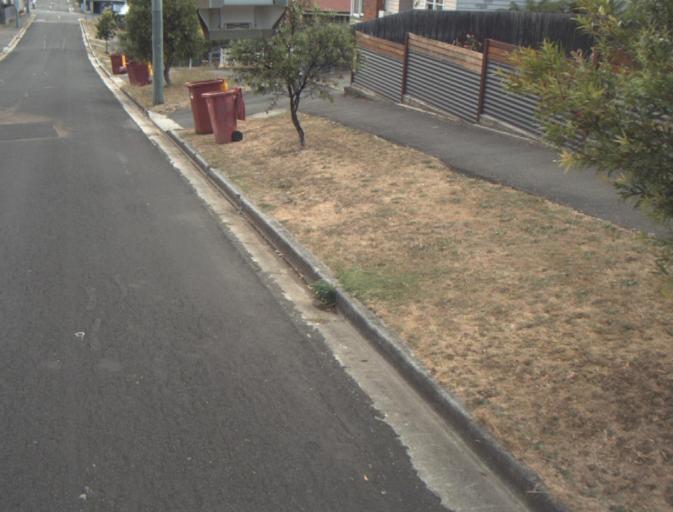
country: AU
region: Tasmania
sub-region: Launceston
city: Newstead
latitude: -41.4576
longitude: 147.2024
